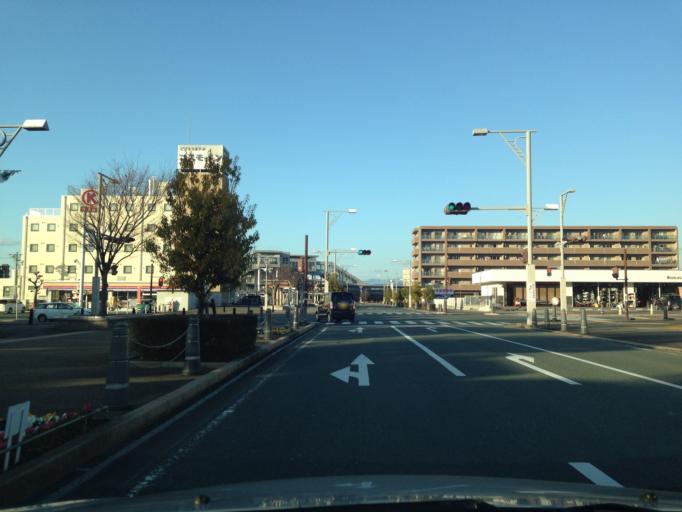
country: JP
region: Shizuoka
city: Fukuroi
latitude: 34.7500
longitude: 137.9622
